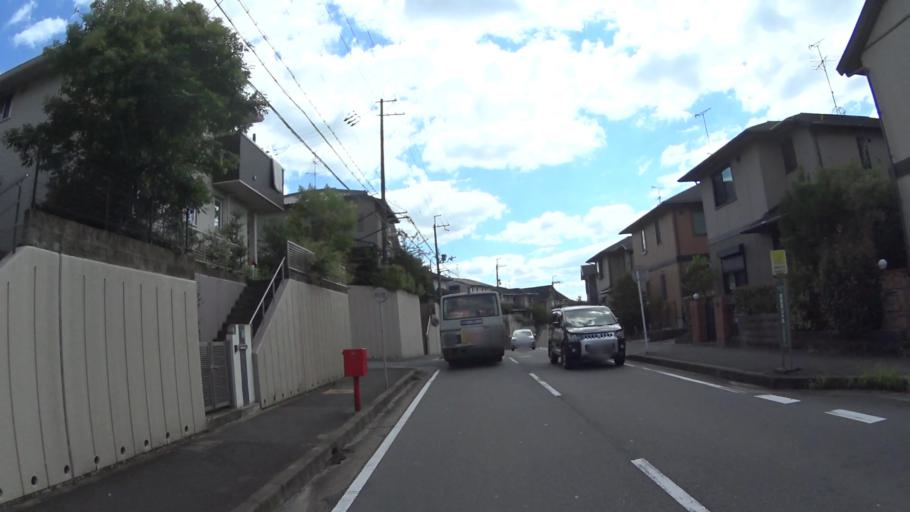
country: JP
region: Kyoto
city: Uji
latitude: 34.9263
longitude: 135.8139
